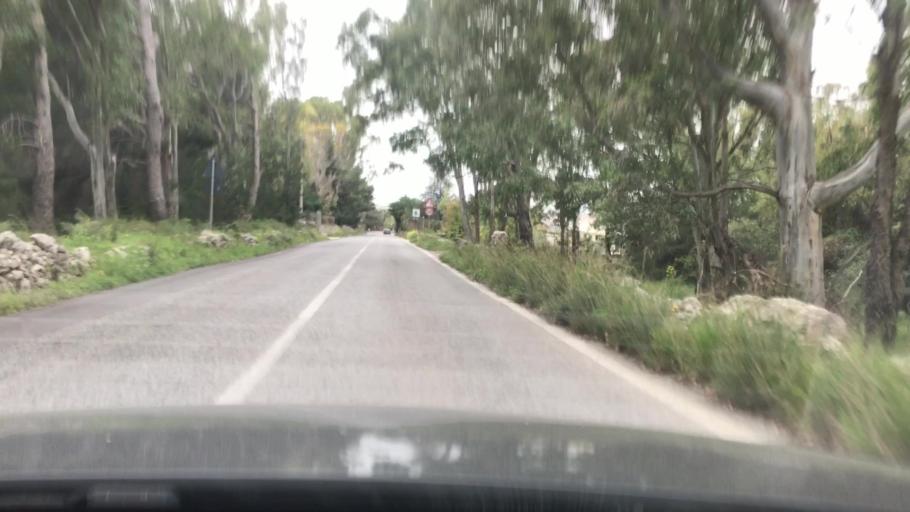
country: IT
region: Sicily
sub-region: Ragusa
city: Scicli
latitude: 36.7990
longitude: 14.7129
